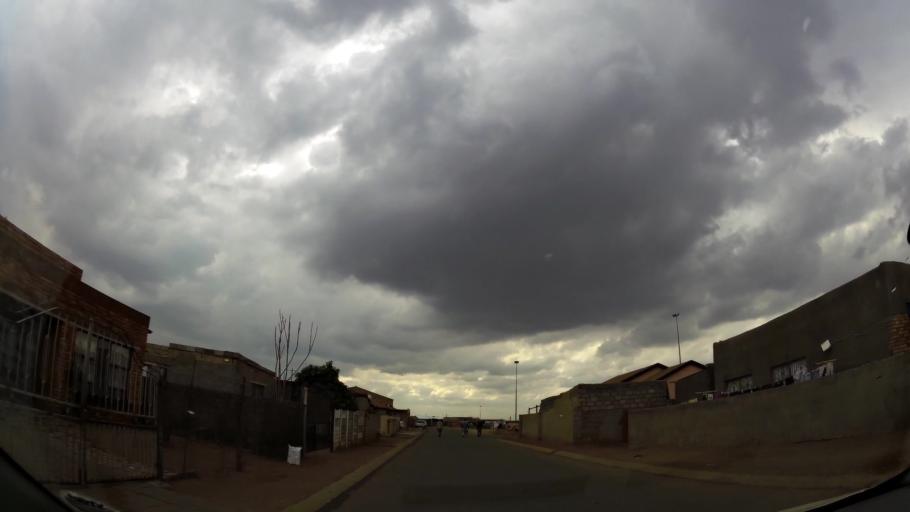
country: ZA
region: Gauteng
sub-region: Ekurhuleni Metropolitan Municipality
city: Germiston
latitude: -26.3678
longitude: 28.1600
